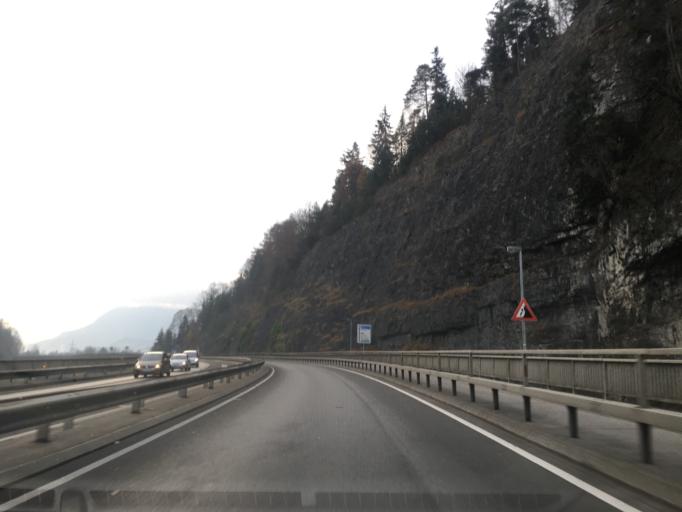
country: AT
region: Vorarlberg
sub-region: Politischer Bezirk Feldkirch
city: Feldkirch
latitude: 47.2322
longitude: 9.6004
